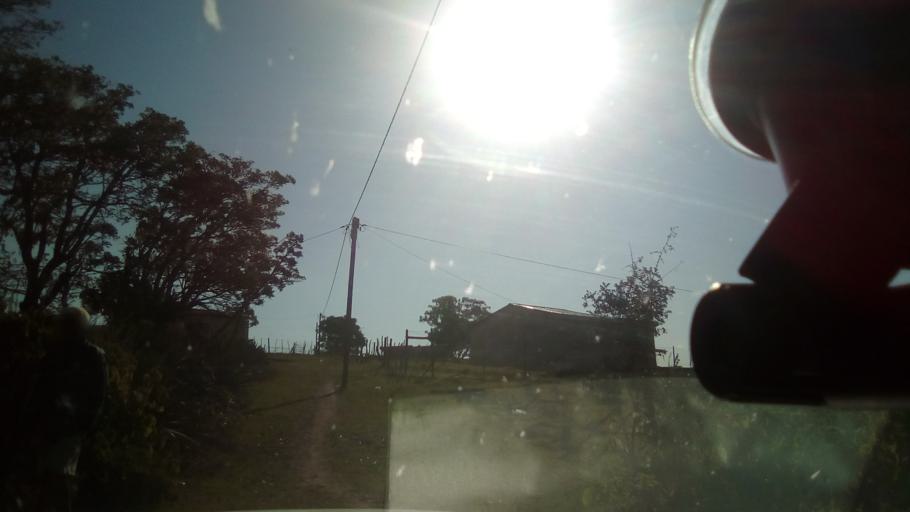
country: ZA
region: Eastern Cape
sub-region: Buffalo City Metropolitan Municipality
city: Bhisho
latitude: -32.7989
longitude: 27.3481
